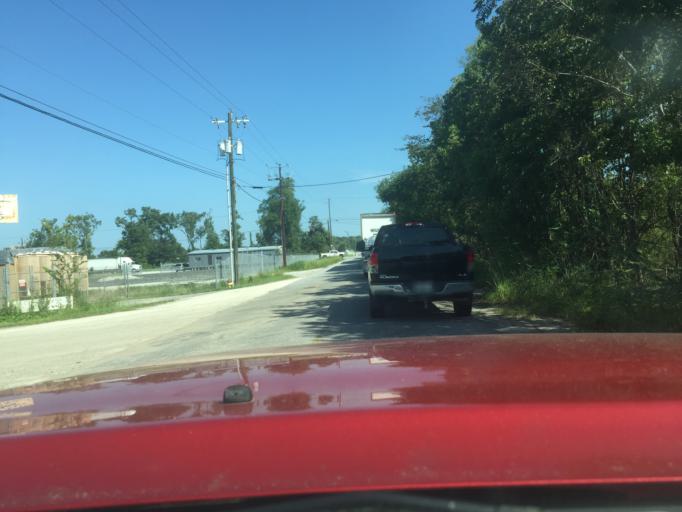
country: US
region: Georgia
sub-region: Chatham County
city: Garden City
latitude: 32.0780
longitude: -81.1454
